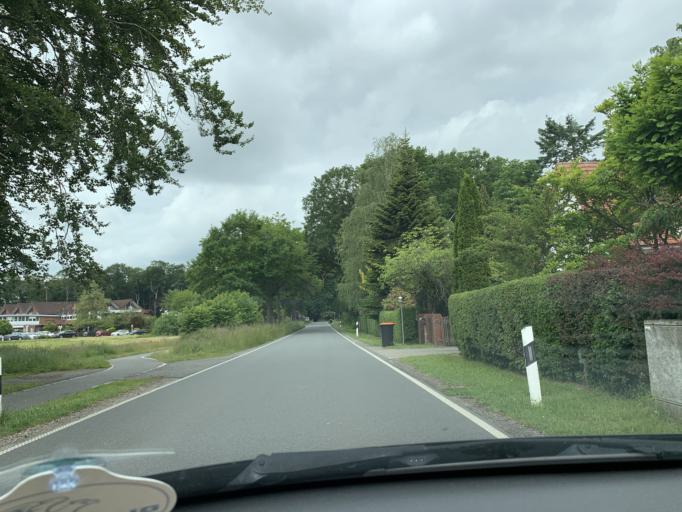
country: DE
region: Lower Saxony
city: Varel
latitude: 53.3762
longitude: 8.0834
